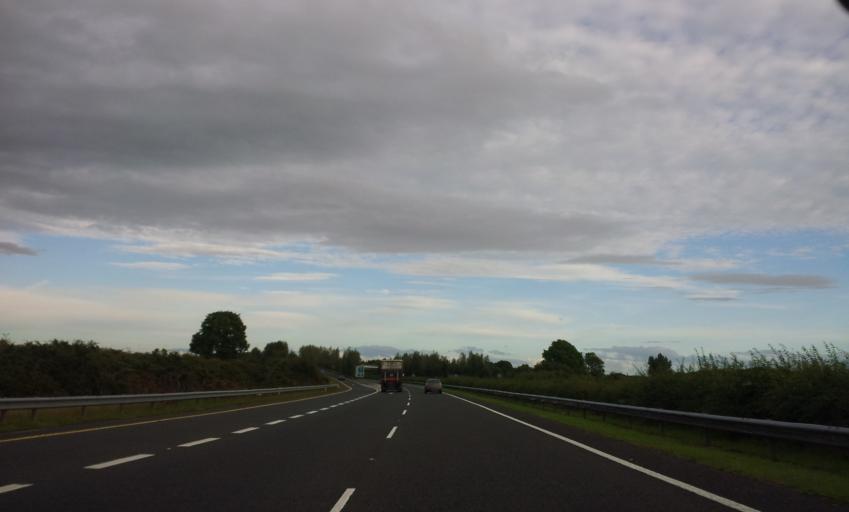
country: IE
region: Munster
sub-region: An Clar
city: Shannon
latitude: 52.7299
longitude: -8.8834
